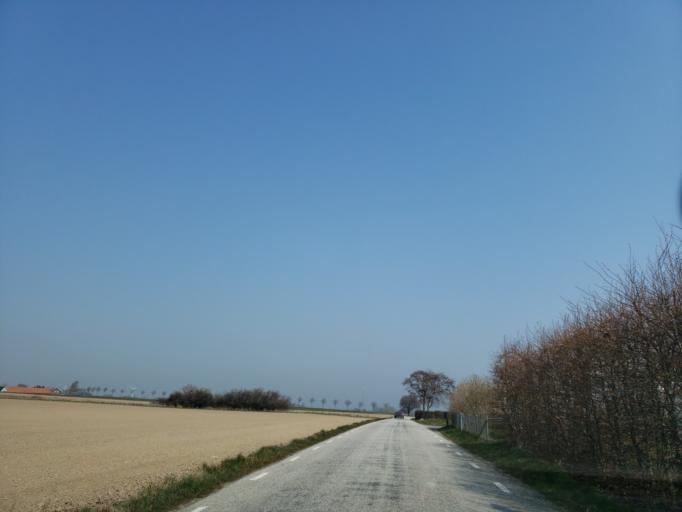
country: SE
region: Skane
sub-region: Simrishamns Kommun
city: Simrishamn
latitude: 55.5096
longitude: 14.3181
